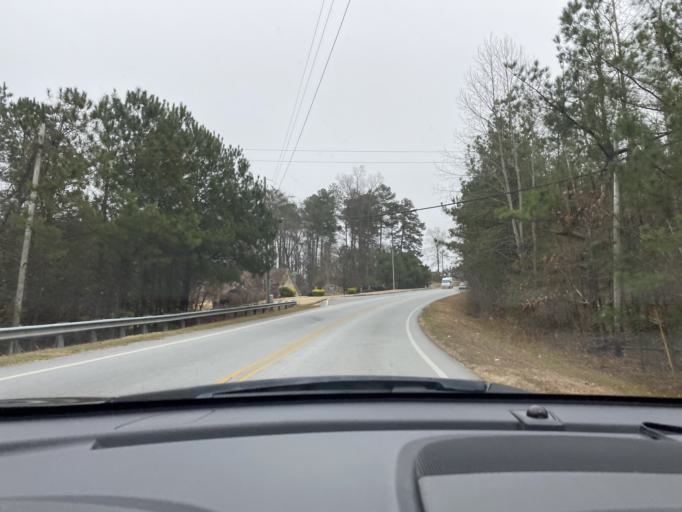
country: US
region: Georgia
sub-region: Gwinnett County
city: Grayson
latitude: 33.9089
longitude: -83.9287
